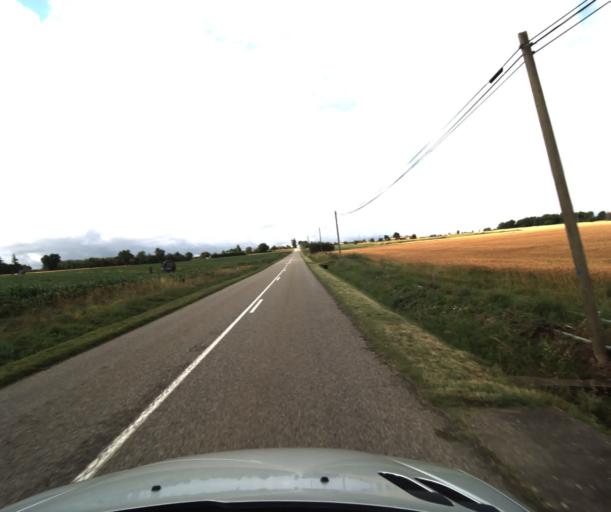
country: FR
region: Midi-Pyrenees
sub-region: Departement du Tarn-et-Garonne
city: Saint-Nicolas-de-la-Grave
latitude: 44.0051
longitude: 0.9906
